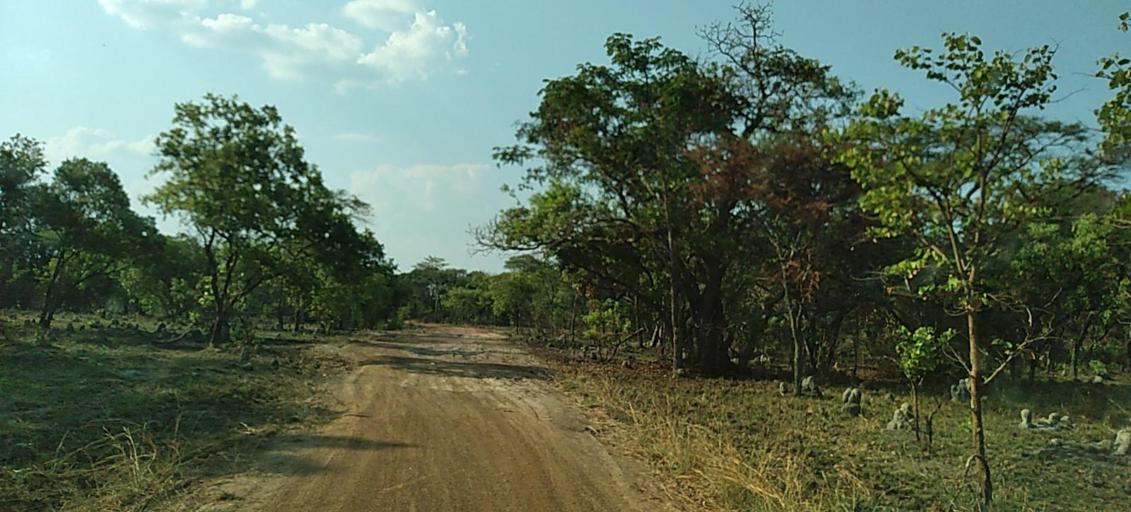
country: ZM
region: Copperbelt
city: Mpongwe
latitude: -13.4404
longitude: 28.0609
